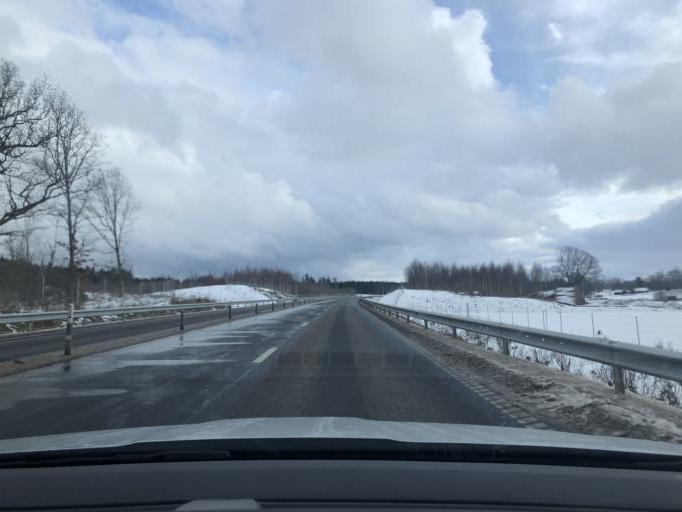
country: SE
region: OEstergoetland
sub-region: Motala Kommun
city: Borensberg
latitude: 58.5894
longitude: 15.1748
